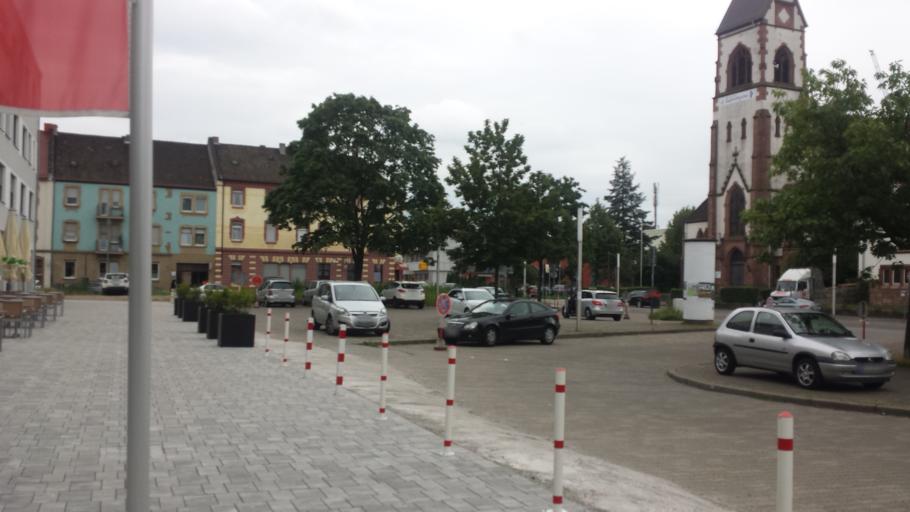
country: DE
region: Baden-Wuerttemberg
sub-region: Karlsruhe Region
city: Mannheim
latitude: 49.5245
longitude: 8.4841
